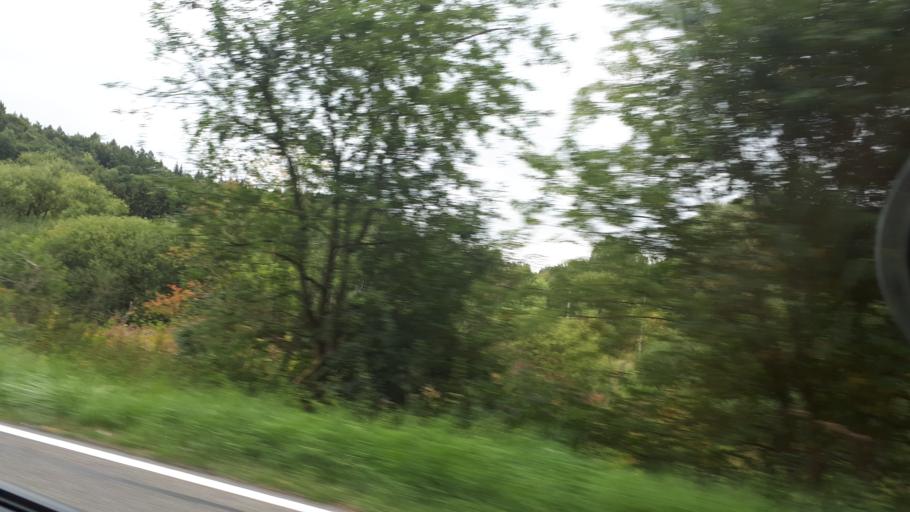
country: DE
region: Saarland
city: Spiesen-Elversberg
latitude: 49.2961
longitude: 7.1602
